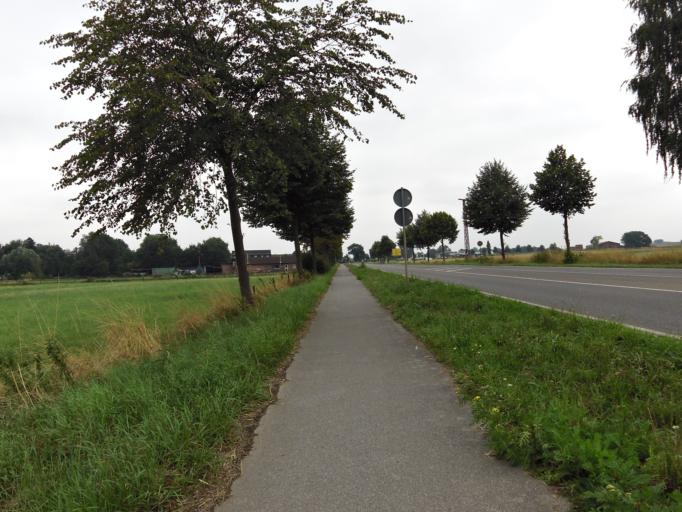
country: DE
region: North Rhine-Westphalia
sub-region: Regierungsbezirk Koln
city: Linnich
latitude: 50.9817
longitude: 6.2600
